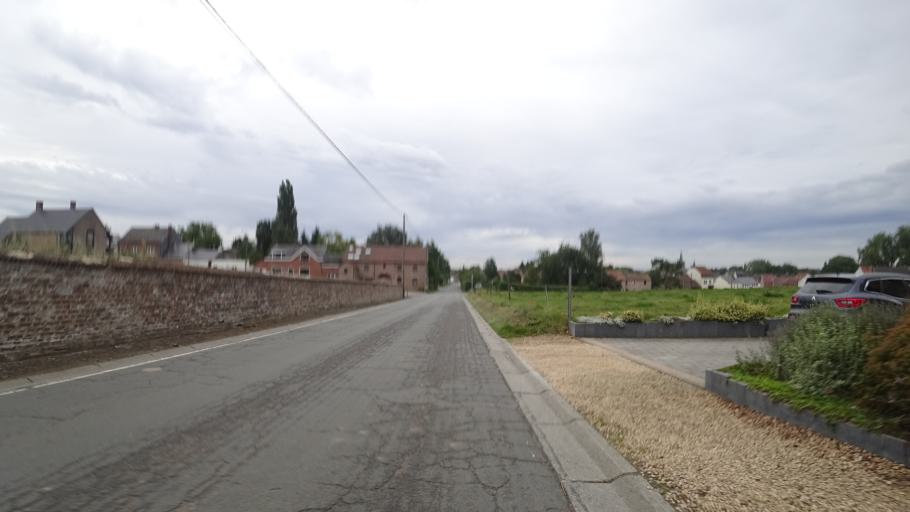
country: BE
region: Wallonia
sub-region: Province du Brabant Wallon
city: Perwez
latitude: 50.5857
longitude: 4.7658
